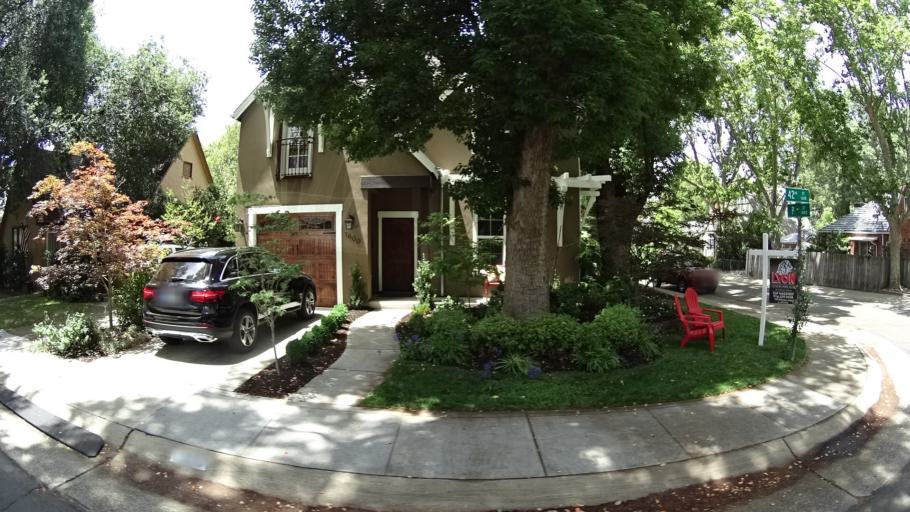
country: US
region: California
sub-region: Sacramento County
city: Sacramento
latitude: 38.5624
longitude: -121.4533
